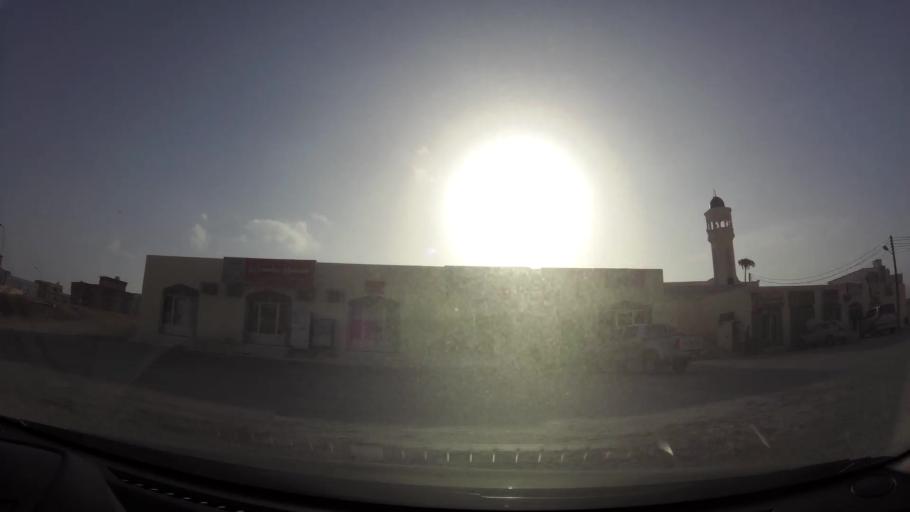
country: OM
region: Zufar
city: Salalah
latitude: 17.0134
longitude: 54.0331
